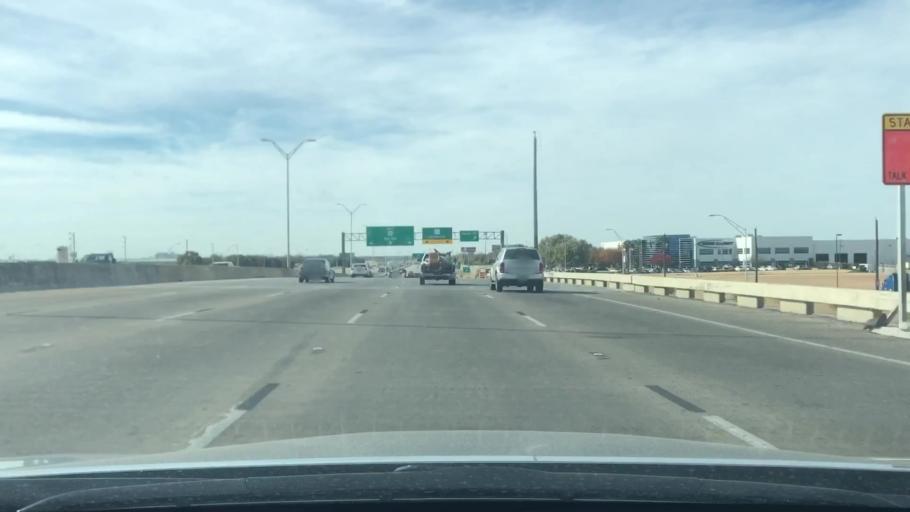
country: US
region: Texas
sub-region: Bexar County
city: Lackland Air Force Base
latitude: 29.4066
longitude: -98.5751
